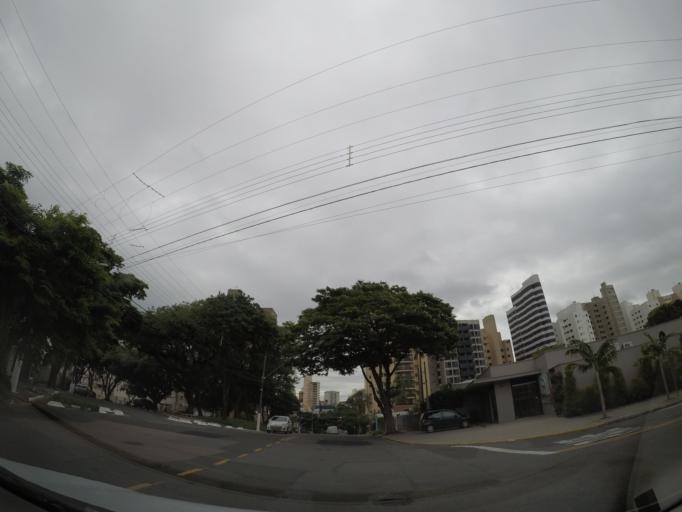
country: BR
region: Sao Paulo
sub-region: Campinas
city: Campinas
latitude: -22.9139
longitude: -47.0424
